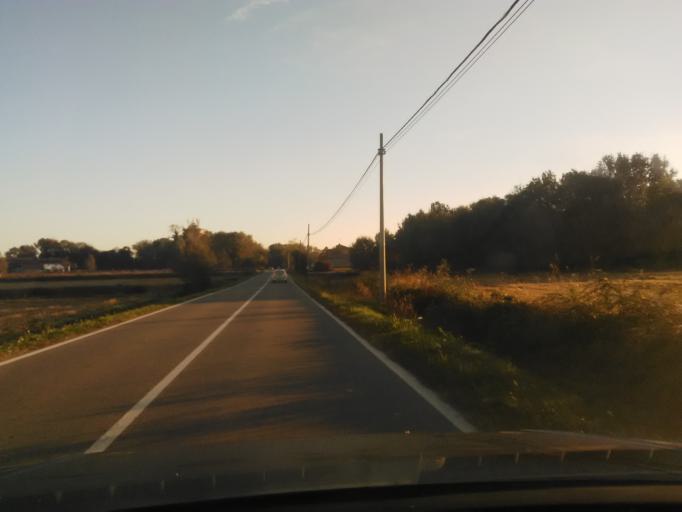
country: IT
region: Piedmont
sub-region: Provincia di Vercelli
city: Carisio
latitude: 45.4030
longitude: 8.1921
